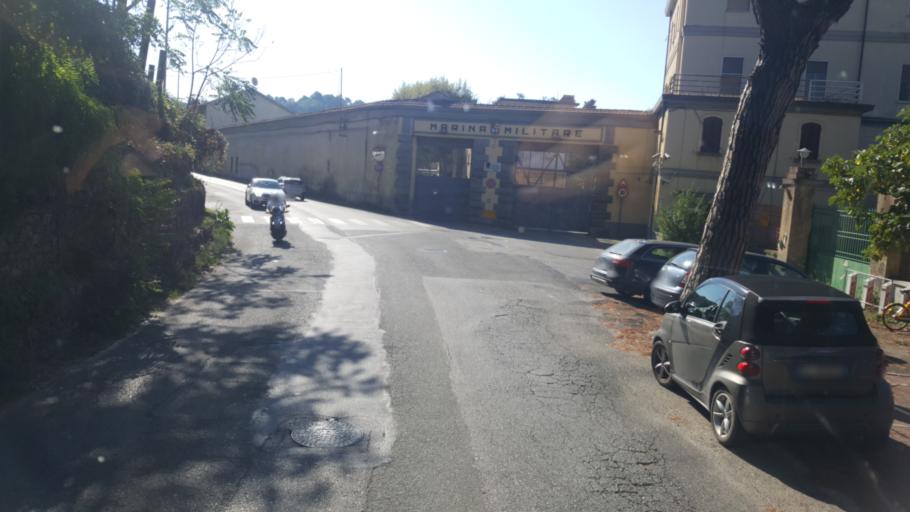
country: IT
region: Liguria
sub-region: Provincia di La Spezia
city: Pitelli
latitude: 44.0989
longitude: 9.8623
